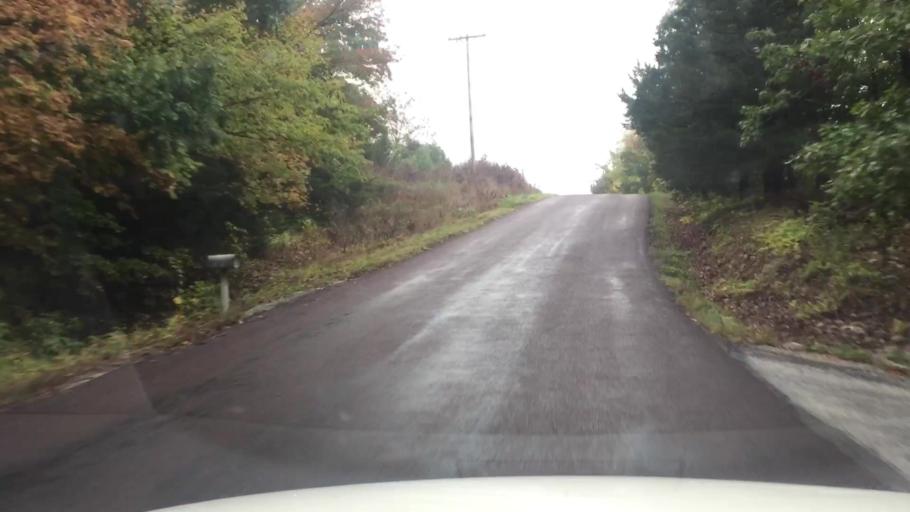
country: US
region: Missouri
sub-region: Boone County
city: Columbia
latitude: 38.8560
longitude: -92.3655
